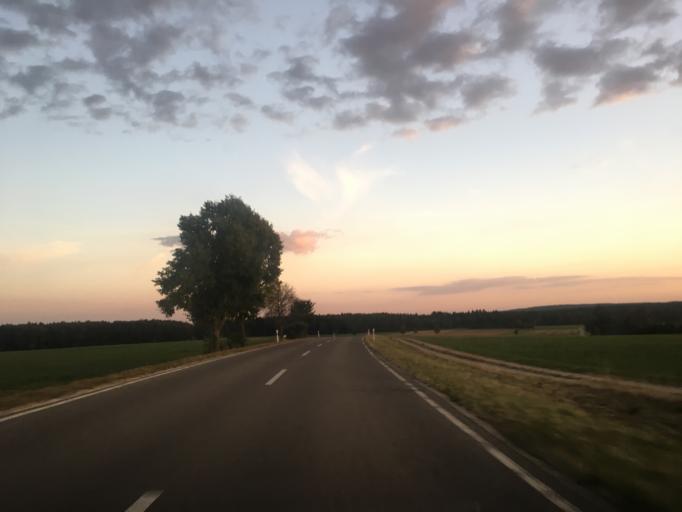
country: DE
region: Baden-Wuerttemberg
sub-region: Tuebingen Region
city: Hayingen
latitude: 48.3108
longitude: 9.4454
